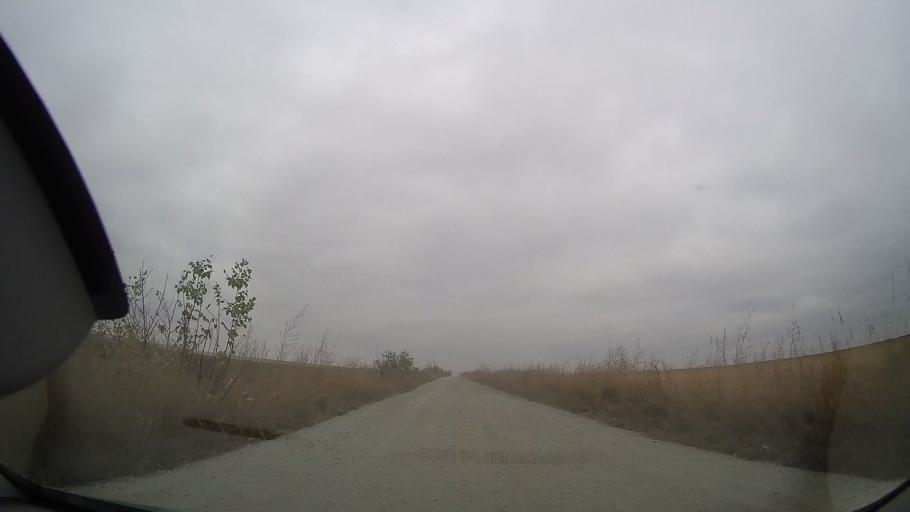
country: RO
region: Ialomita
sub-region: Comuna Grivita
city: Grivita
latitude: 44.7448
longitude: 27.2695
